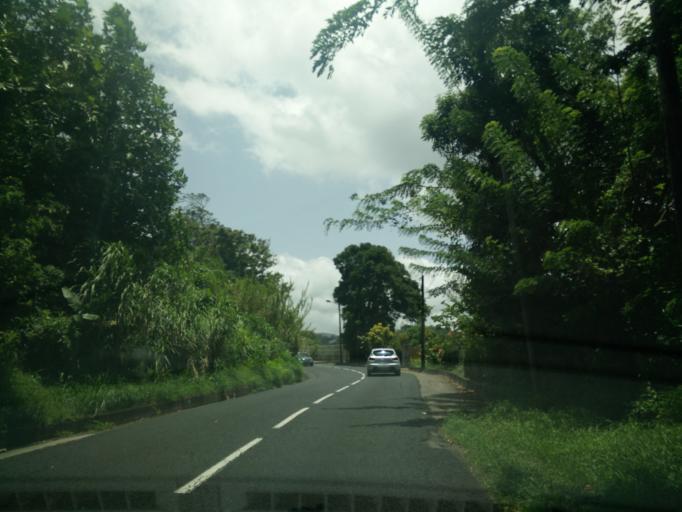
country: MQ
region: Martinique
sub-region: Martinique
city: Fort-de-France
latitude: 14.6366
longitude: -61.0720
